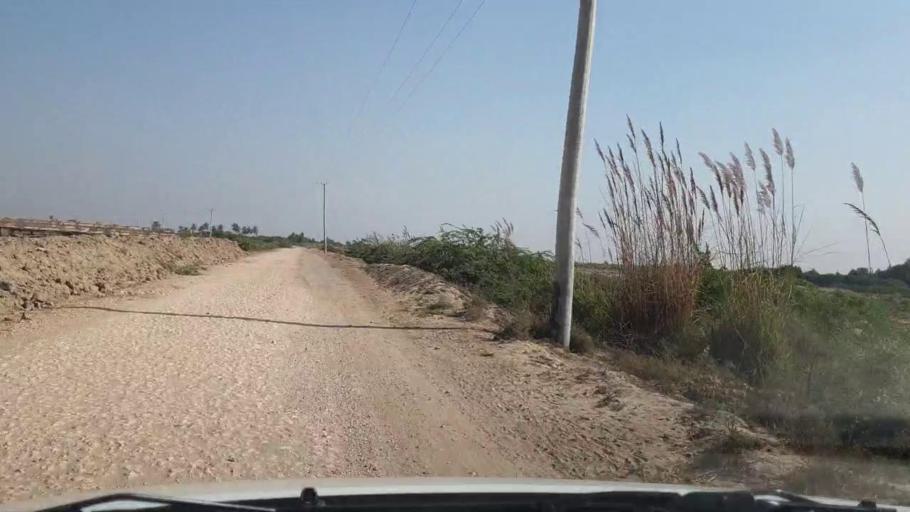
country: PK
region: Sindh
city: Mirpur Sakro
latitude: 24.6483
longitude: 67.6300
